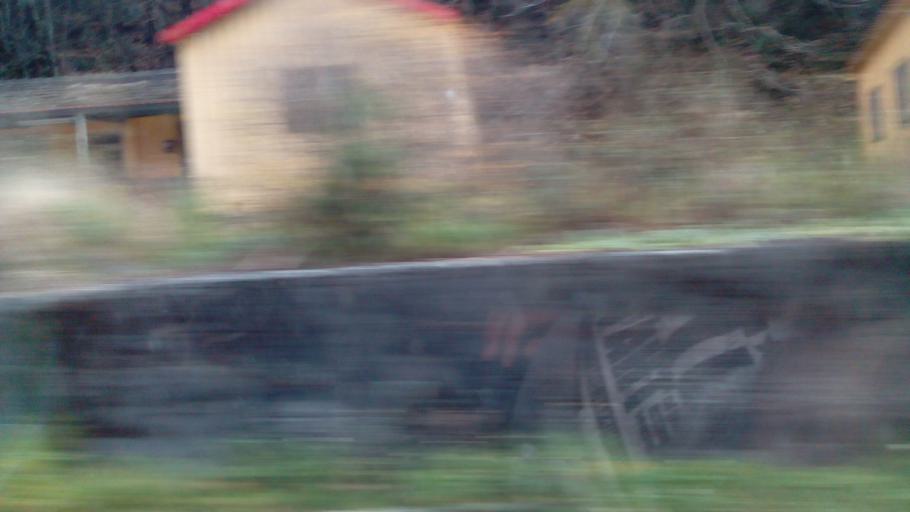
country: TW
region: Taiwan
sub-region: Hualien
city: Hualian
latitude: 24.3548
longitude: 121.3253
